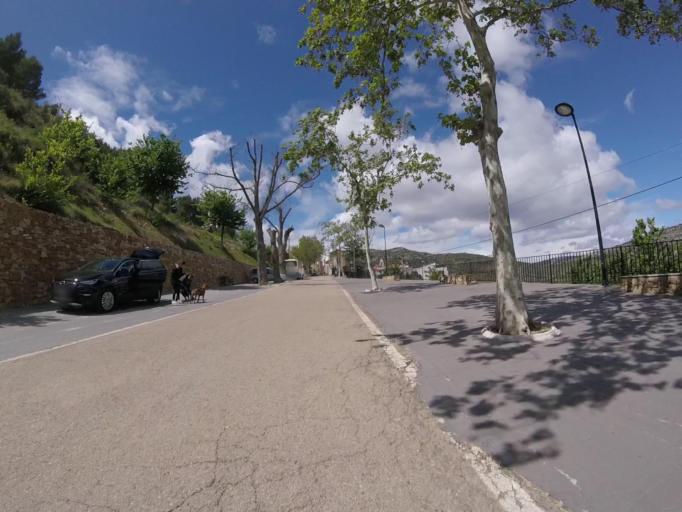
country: ES
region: Valencia
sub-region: Provincia de Castello
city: Sierra-Engarceran
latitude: 40.2700
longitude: -0.0158
